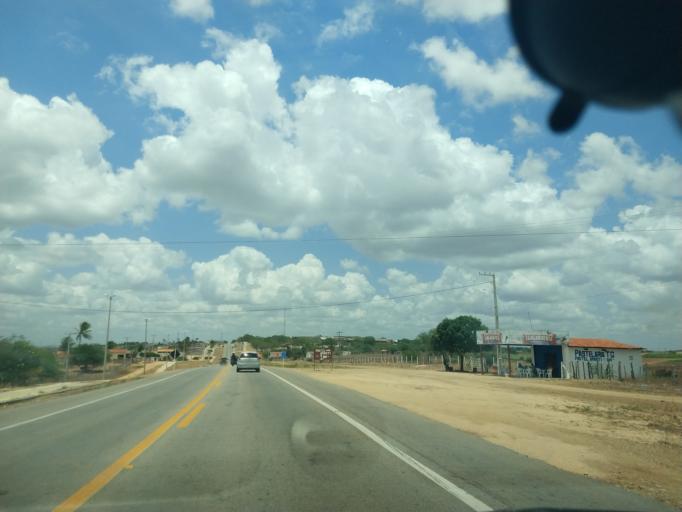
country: BR
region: Rio Grande do Norte
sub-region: Tangara
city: Tangara
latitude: -6.1911
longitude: -35.7904
